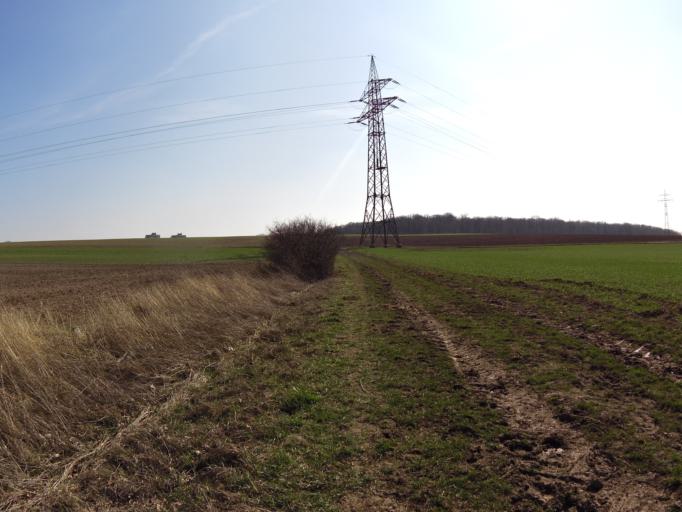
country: DE
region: Bavaria
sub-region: Regierungsbezirk Unterfranken
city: Rottendorf
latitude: 49.8054
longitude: 10.0172
